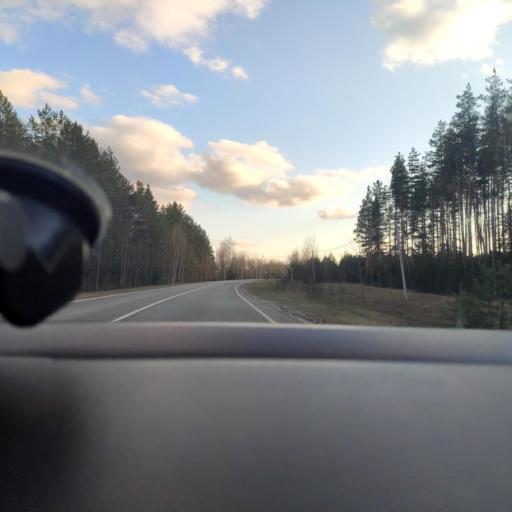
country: RU
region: Moskovskaya
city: Shaturtorf
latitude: 55.4396
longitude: 39.4323
